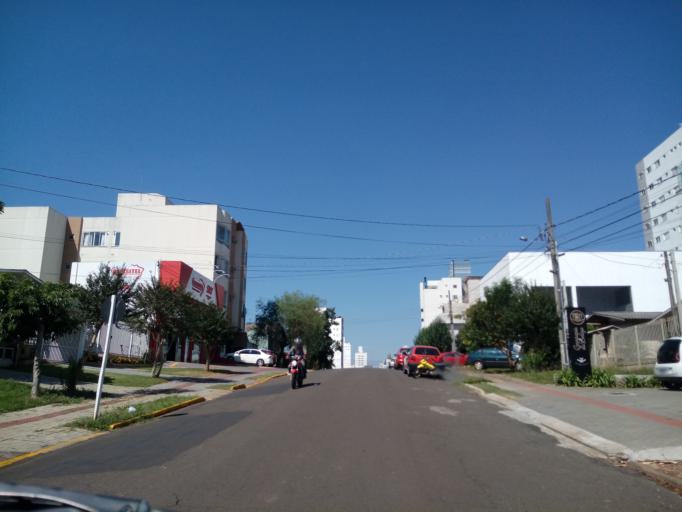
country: BR
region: Santa Catarina
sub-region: Chapeco
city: Chapeco
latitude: -27.0945
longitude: -52.6120
